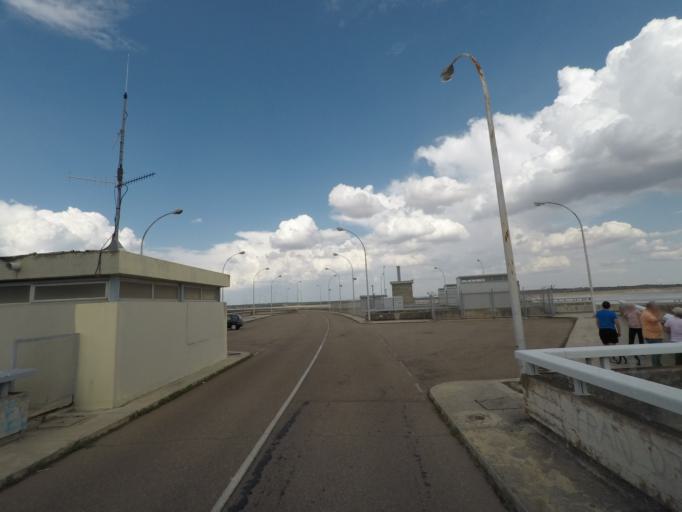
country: ES
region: Castille and Leon
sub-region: Provincia de Salamanca
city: Almendra
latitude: 41.2686
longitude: -6.3210
